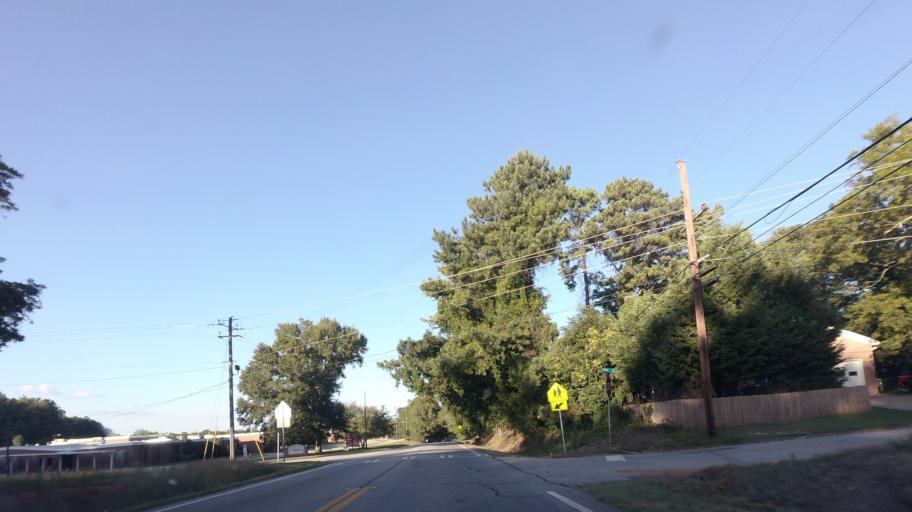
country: US
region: Georgia
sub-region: Spalding County
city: East Griffin
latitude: 33.2545
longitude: -84.2403
